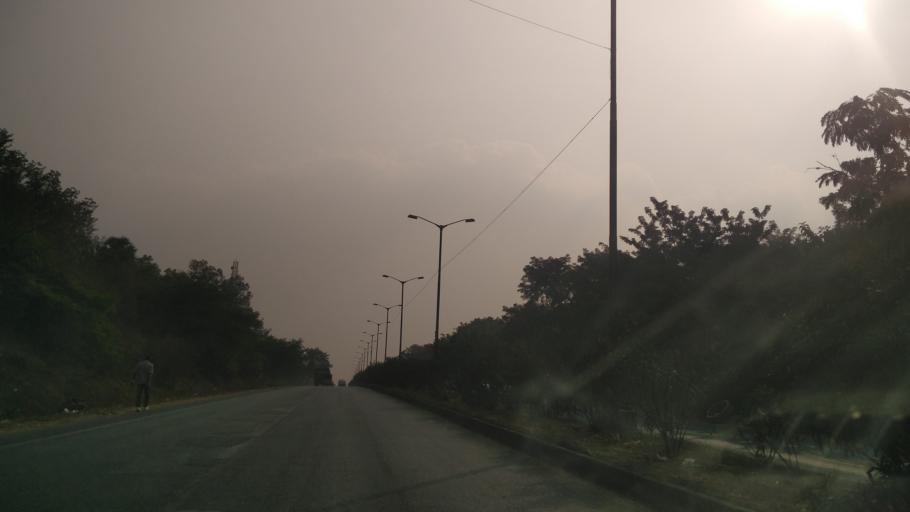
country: IN
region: Andhra Pradesh
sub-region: East Godavari
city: Rajahmundry
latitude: 16.9647
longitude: 81.7960
